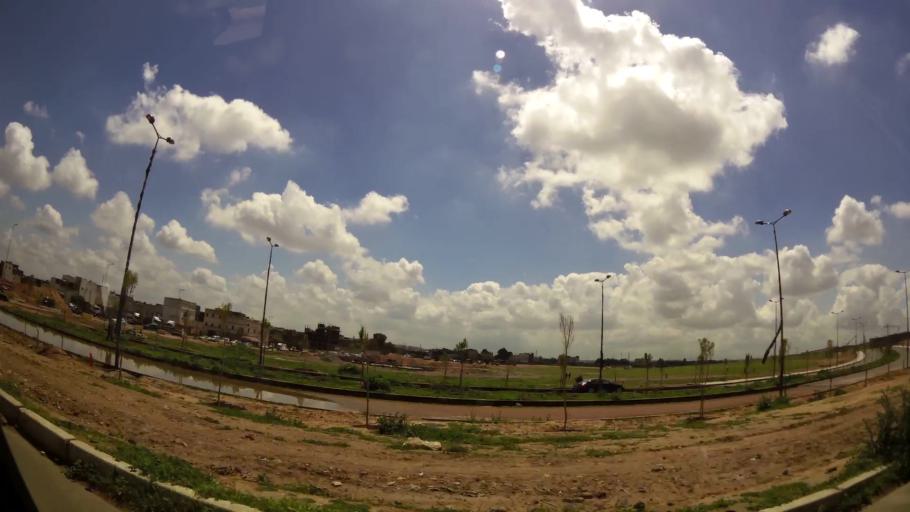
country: MA
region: Grand Casablanca
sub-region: Mediouna
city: Tit Mellil
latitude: 33.5432
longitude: -7.5438
